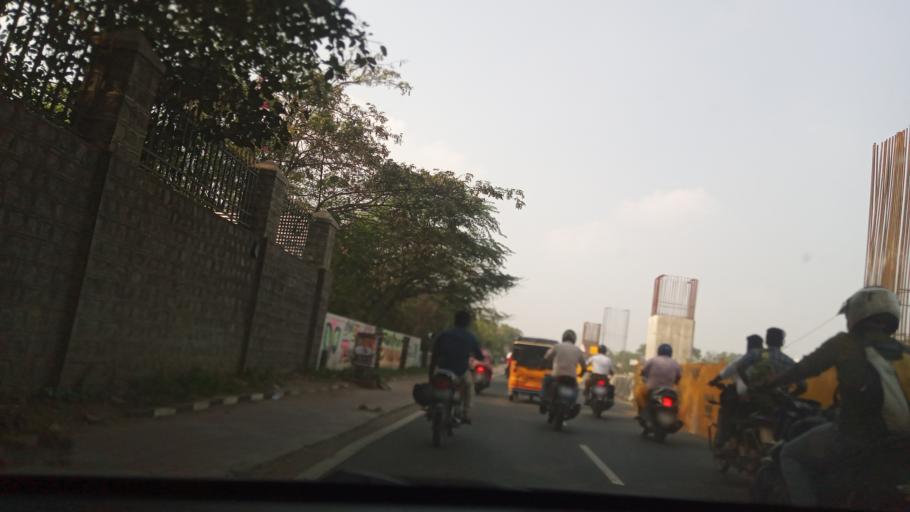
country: IN
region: Tamil Nadu
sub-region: Coimbatore
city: Singanallur
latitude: 11.0334
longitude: 77.0321
